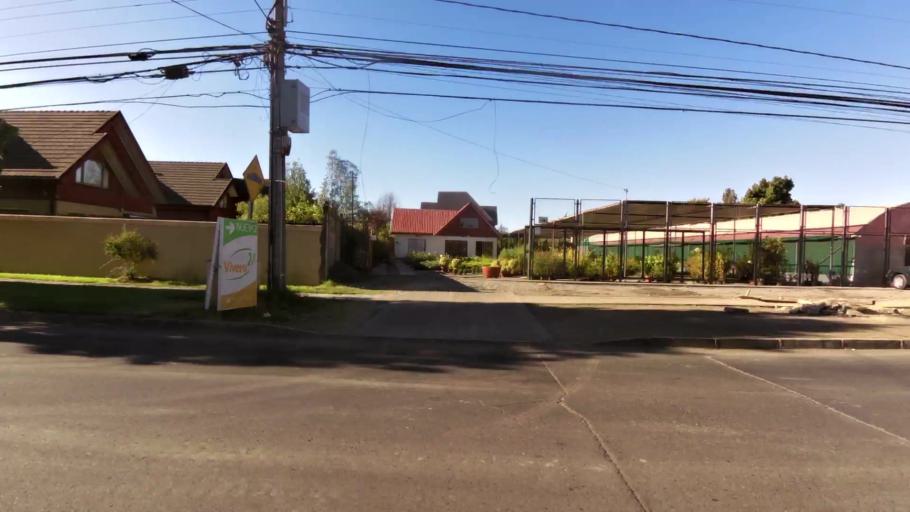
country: CL
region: Biobio
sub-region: Provincia de Concepcion
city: Concepcion
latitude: -36.8370
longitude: -73.1031
